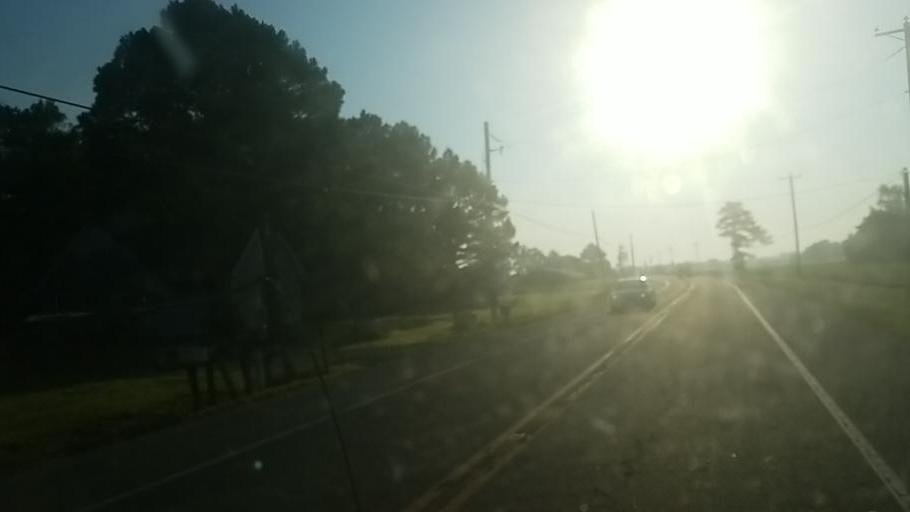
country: US
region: Delaware
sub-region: Sussex County
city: Selbyville
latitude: 38.4626
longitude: -75.1862
